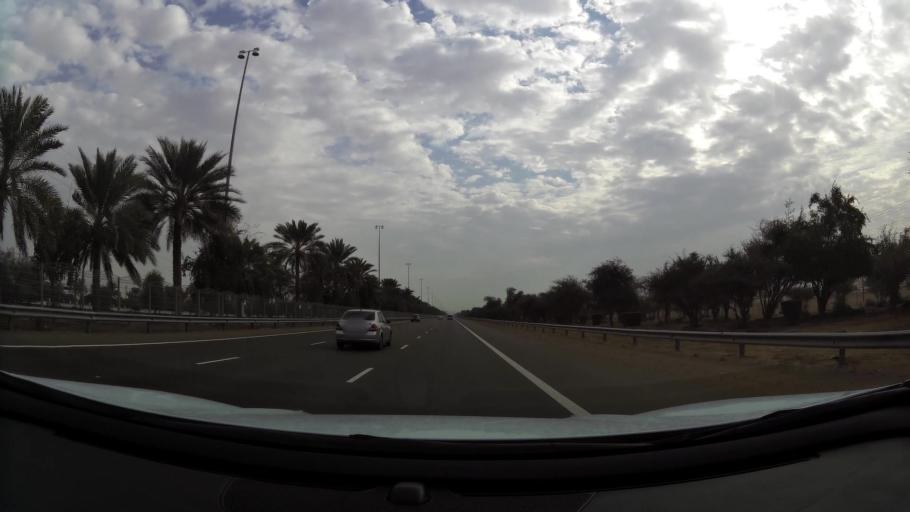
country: AE
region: Abu Dhabi
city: Al Ain
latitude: 24.2166
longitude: 55.5351
